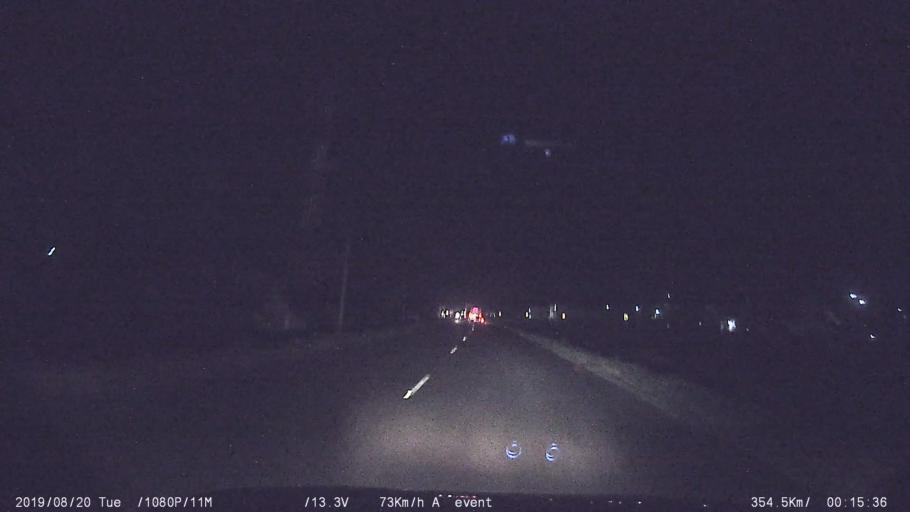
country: IN
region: Tamil Nadu
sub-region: Salem
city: Ilampillai
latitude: 11.5479
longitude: 77.9909
